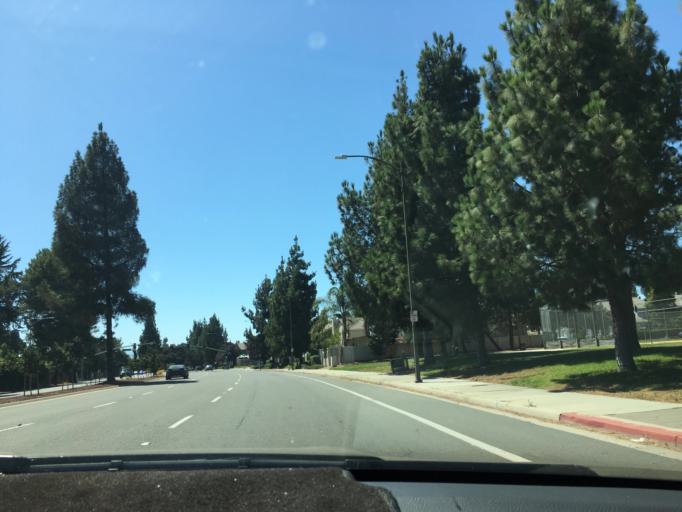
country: US
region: California
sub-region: Santa Clara County
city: Seven Trees
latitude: 37.2368
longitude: -121.7942
